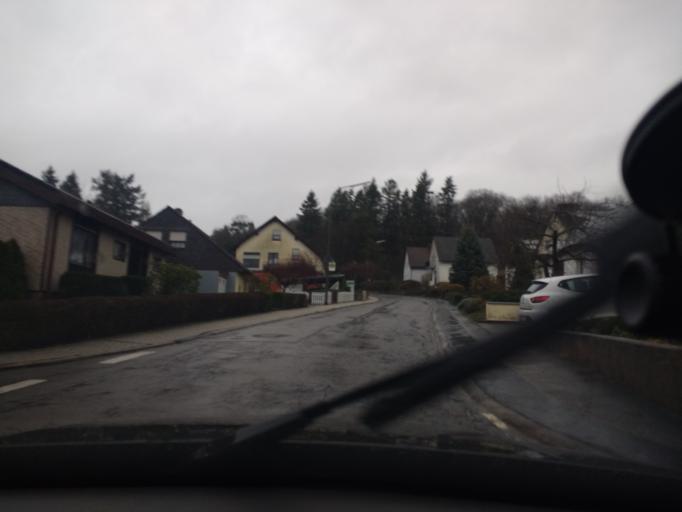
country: DE
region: Rheinland-Pfalz
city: Wiltingen
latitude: 49.6657
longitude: 6.6240
